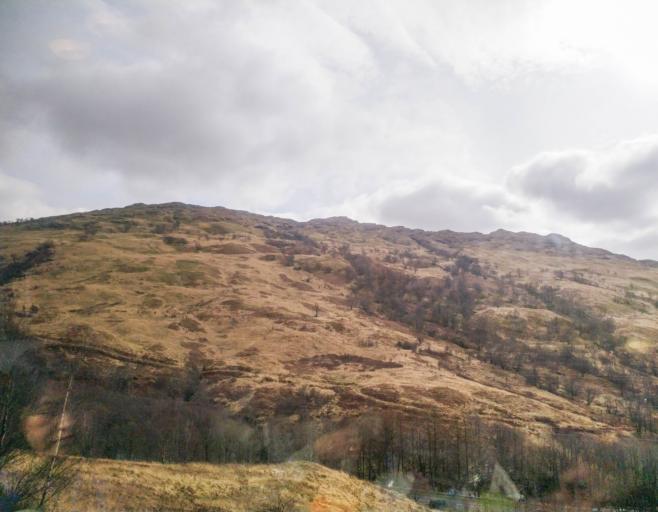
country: GB
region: Scotland
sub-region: Argyll and Bute
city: Garelochhead
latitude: 56.3513
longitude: -4.6966
